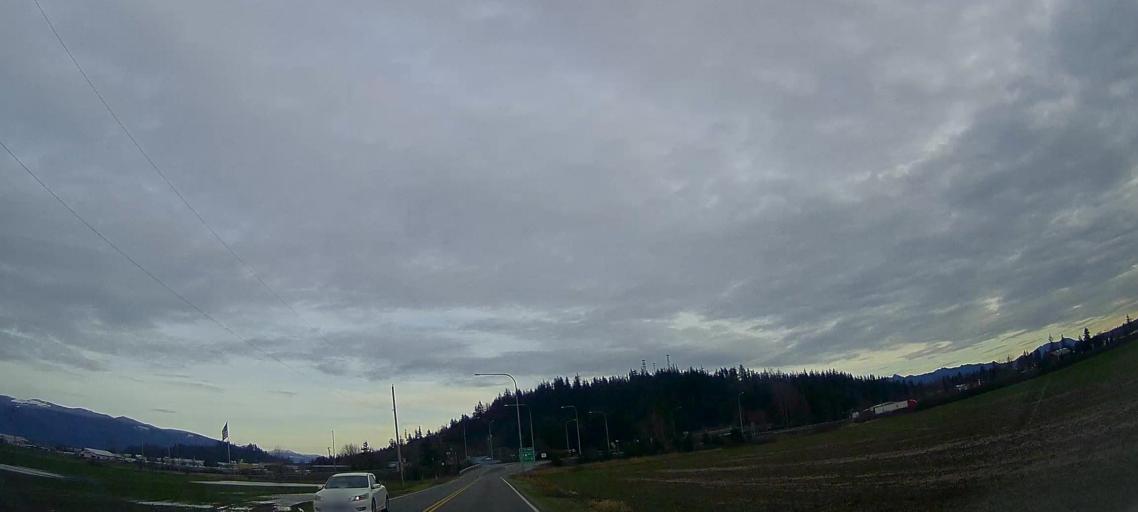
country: US
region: Washington
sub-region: Skagit County
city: Burlington
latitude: 48.4861
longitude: -122.3413
